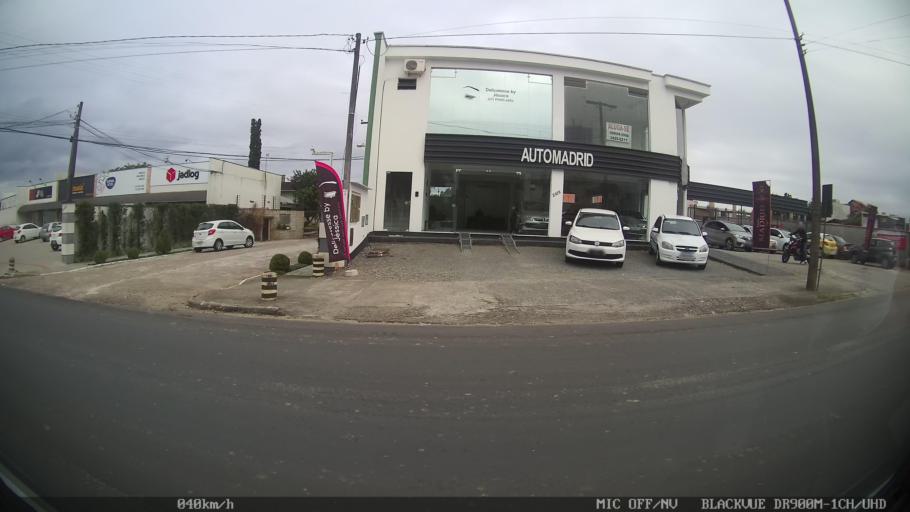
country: BR
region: Santa Catarina
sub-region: Joinville
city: Joinville
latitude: -26.2847
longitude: -48.8732
